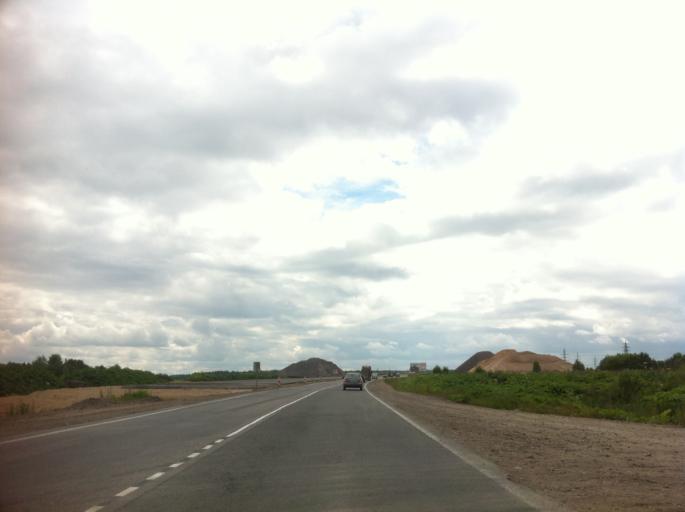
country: RU
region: Leningrad
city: Gatchina
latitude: 59.5439
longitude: 30.1636
